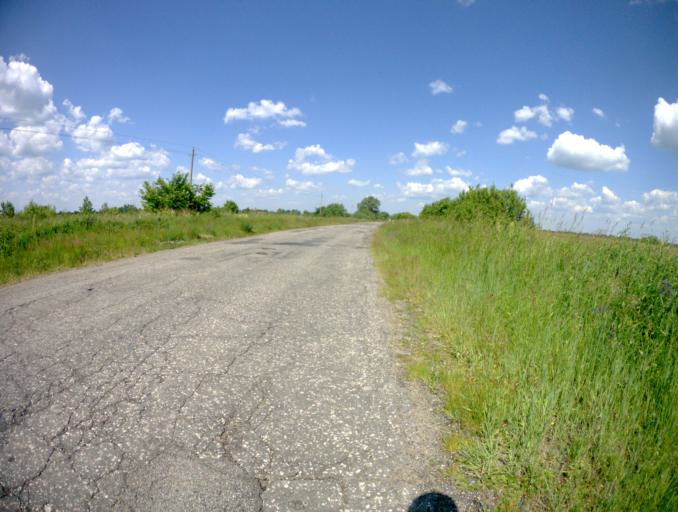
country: RU
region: Vladimir
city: Vyazniki
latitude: 56.2871
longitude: 42.1408
